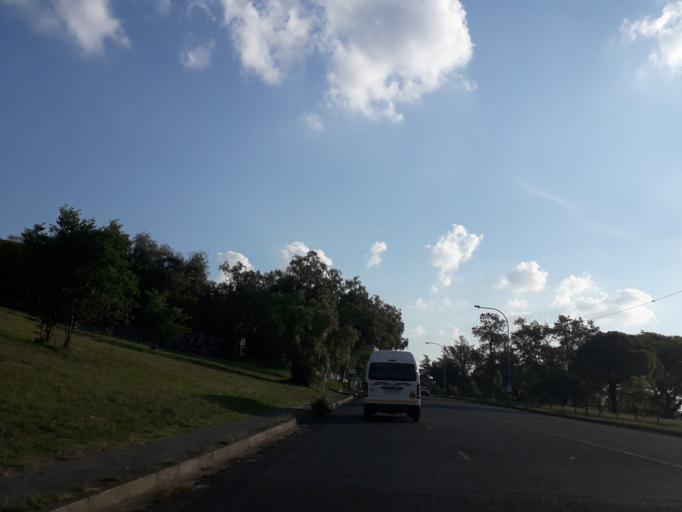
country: ZA
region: Gauteng
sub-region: City of Johannesburg Metropolitan Municipality
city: Johannesburg
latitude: -26.1404
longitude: 28.0097
